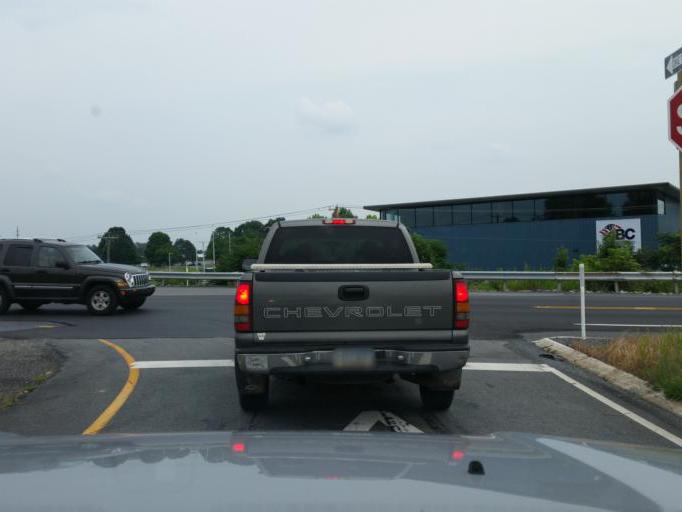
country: US
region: Pennsylvania
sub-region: Lancaster County
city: Mount Joy
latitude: 40.1244
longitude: -76.4707
